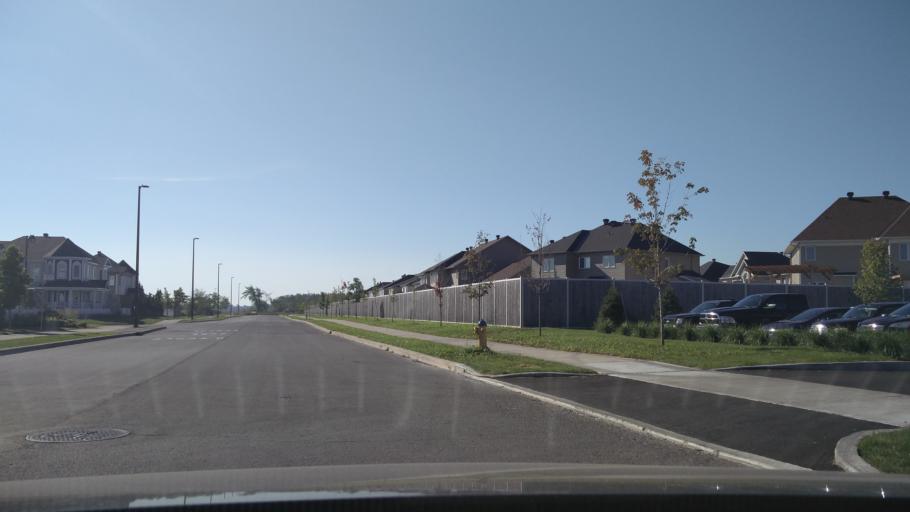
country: CA
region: Ontario
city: Clarence-Rockland
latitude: 45.4502
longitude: -75.4625
